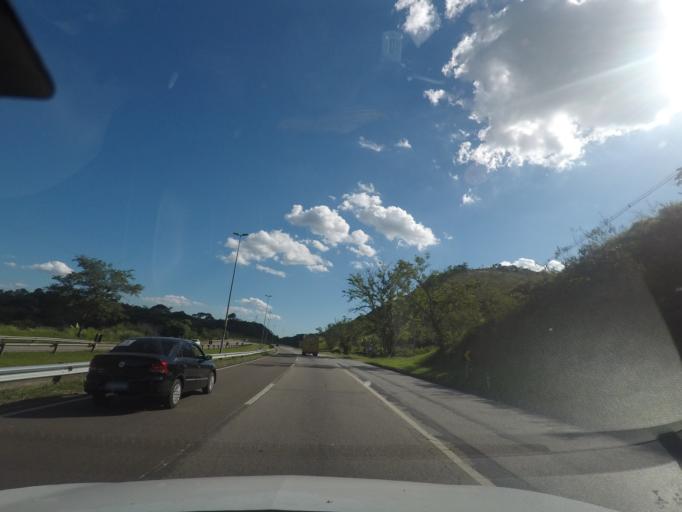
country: BR
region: Rio de Janeiro
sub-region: Guapimirim
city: Guapimirim
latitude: -22.5751
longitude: -43.0096
